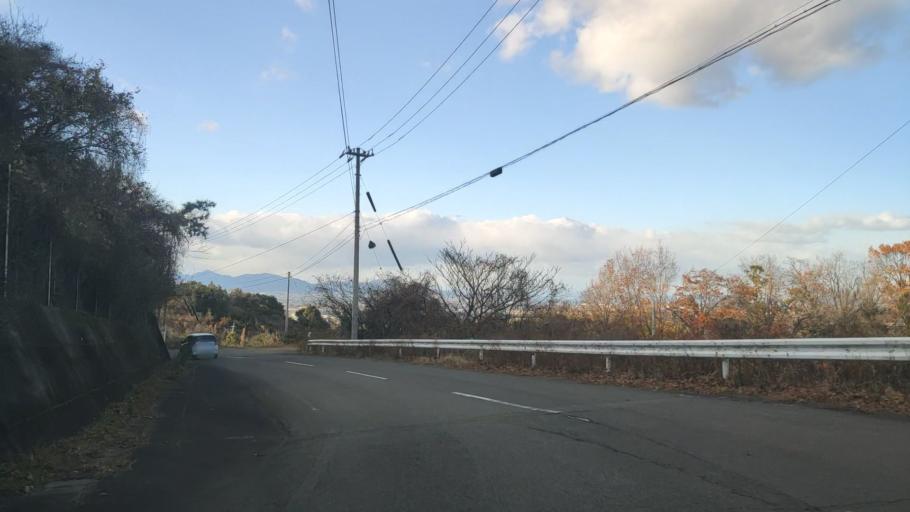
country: JP
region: Ehime
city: Saijo
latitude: 33.8833
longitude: 133.1327
